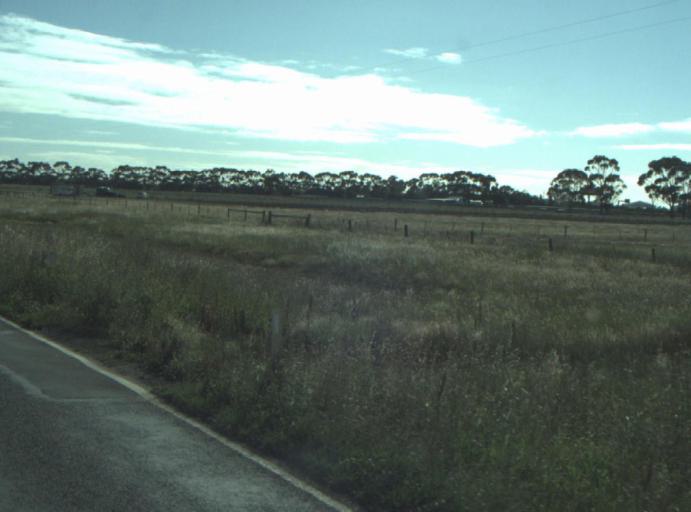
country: AU
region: Victoria
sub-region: Greater Geelong
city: Lara
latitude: -38.0196
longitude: 144.4442
